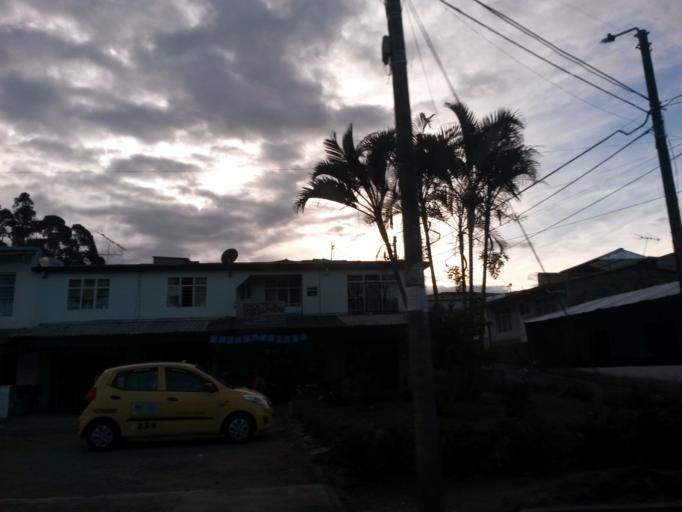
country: CO
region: Cauca
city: Popayan
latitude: 2.4564
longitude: -76.6329
